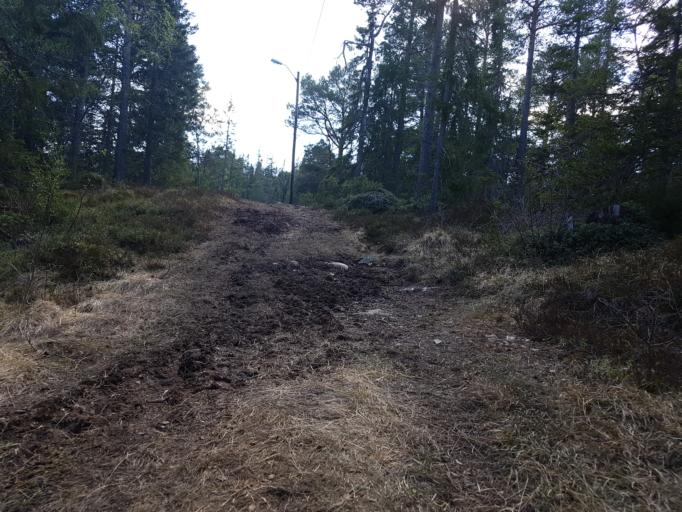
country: NO
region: Sor-Trondelag
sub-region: Trondheim
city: Trondheim
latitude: 63.4461
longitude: 10.2942
